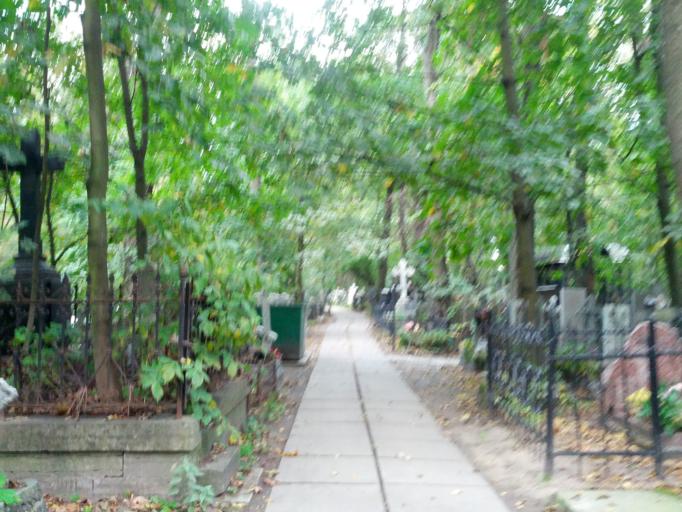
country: RU
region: St.-Petersburg
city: Krasnogvargeisky
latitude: 59.9459
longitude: 30.4243
